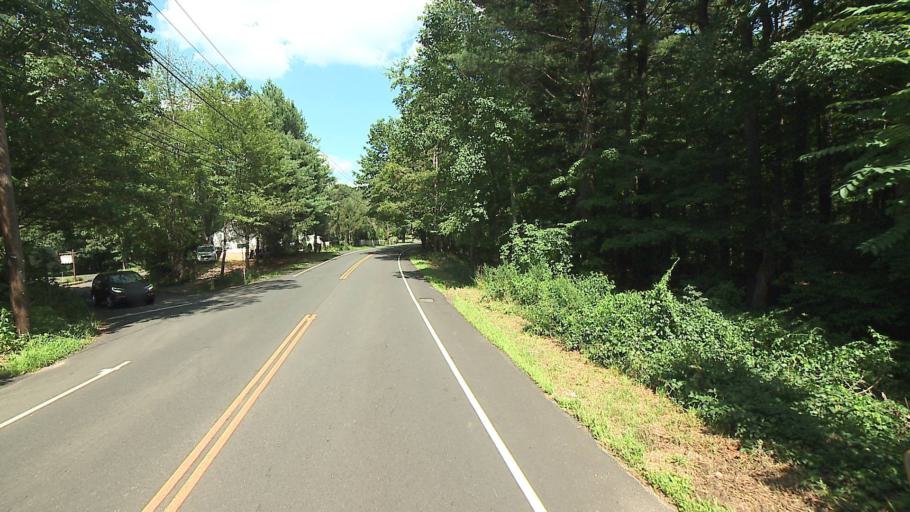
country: US
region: Connecticut
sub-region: Fairfield County
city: Shelton
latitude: 41.3044
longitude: -73.1301
